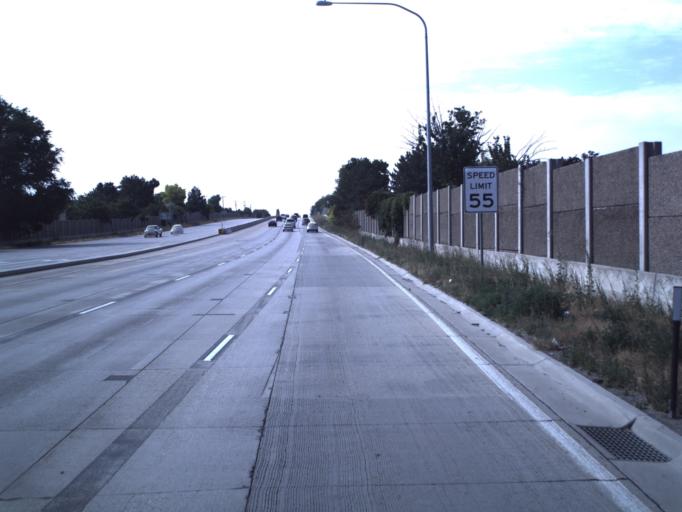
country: US
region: Utah
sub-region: Salt Lake County
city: West Valley City
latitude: 40.6798
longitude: -111.9818
